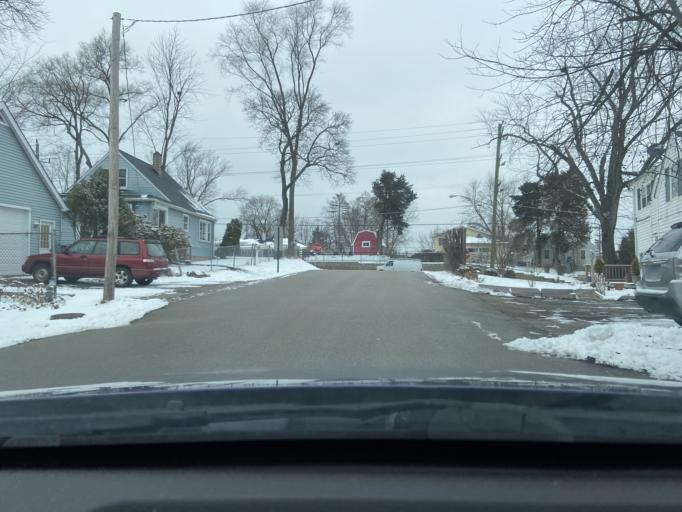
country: US
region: Illinois
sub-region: Lake County
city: Round Lake Park
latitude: 42.3579
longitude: -88.0805
